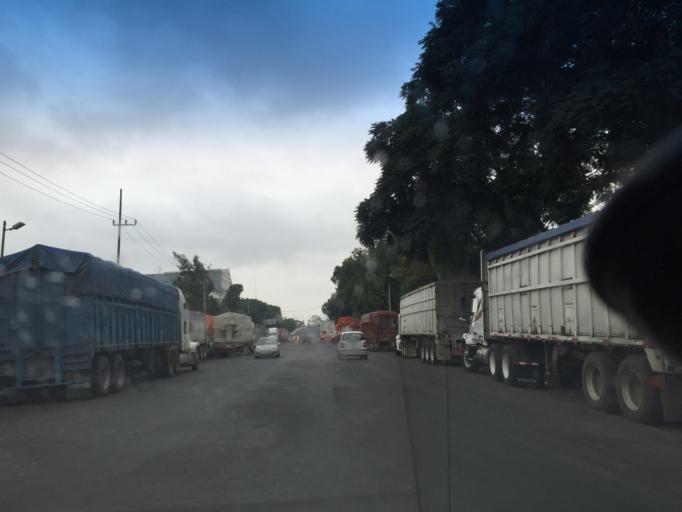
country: MX
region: Mexico City
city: Azcapotzalco
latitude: 19.4981
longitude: -99.1671
